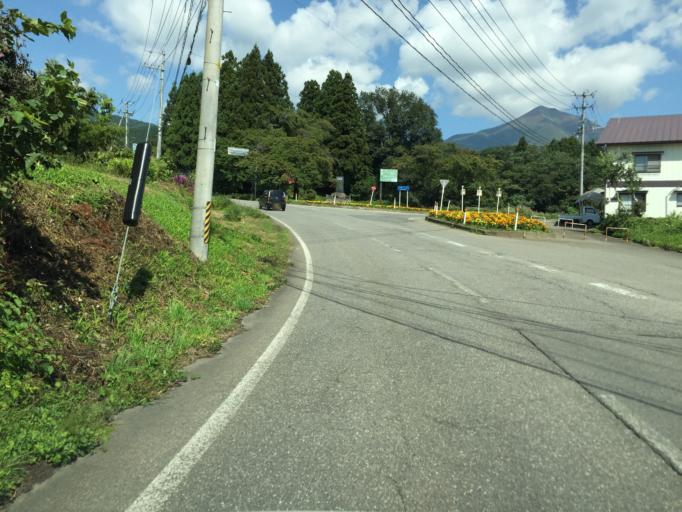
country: JP
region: Fukushima
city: Inawashiro
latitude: 37.5689
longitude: 140.0185
